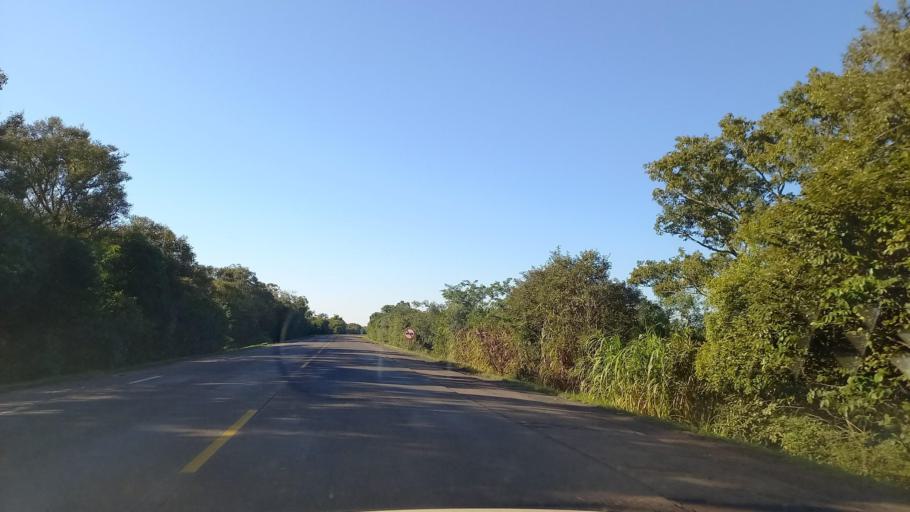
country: BR
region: Rio Grande do Sul
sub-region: Venancio Aires
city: Venancio Aires
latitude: -29.6765
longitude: -52.0129
